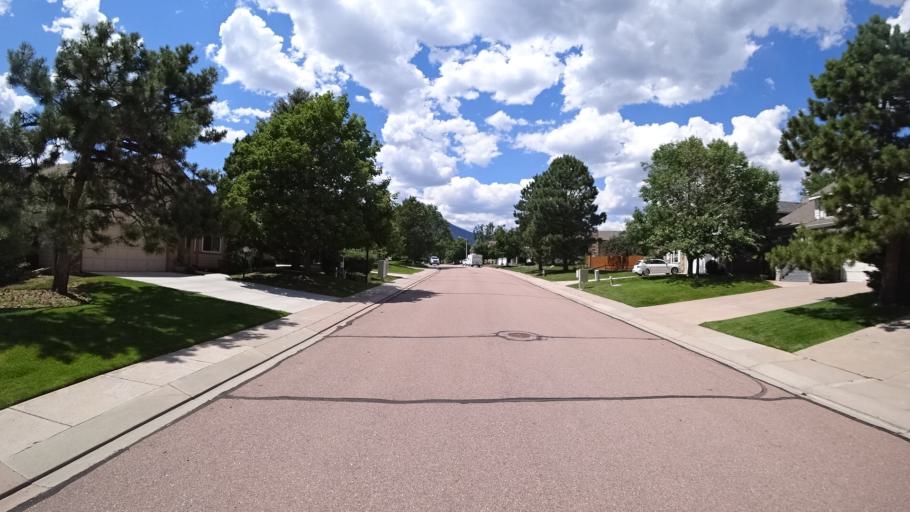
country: US
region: Colorado
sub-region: El Paso County
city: Air Force Academy
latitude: 38.9428
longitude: -104.8479
